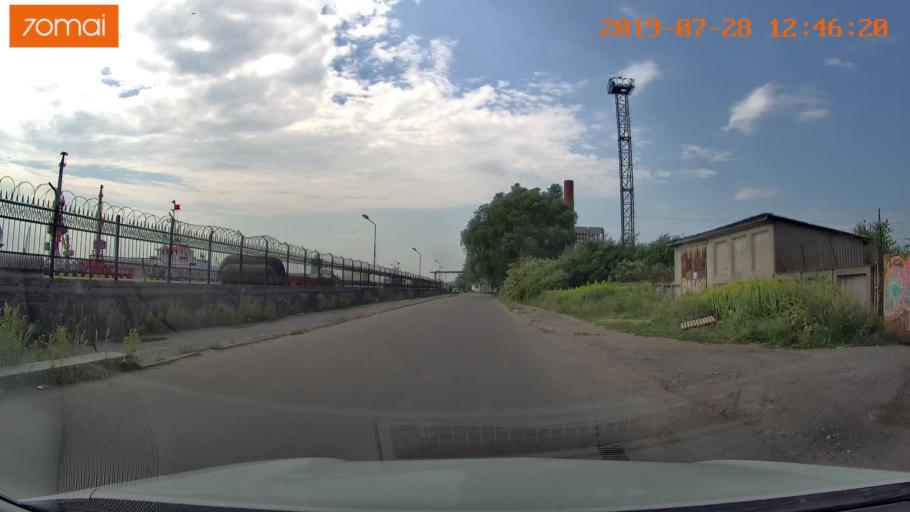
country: RU
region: Kaliningrad
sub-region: Gorod Kaliningrad
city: Kaliningrad
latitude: 54.7064
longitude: 20.4567
